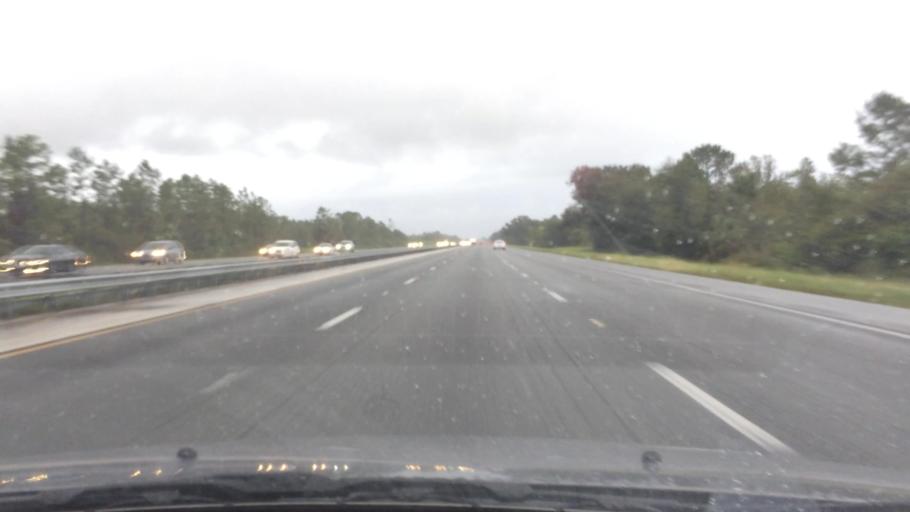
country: US
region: Florida
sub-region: Volusia County
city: Ormond-by-the-Sea
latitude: 29.3109
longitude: -81.1316
